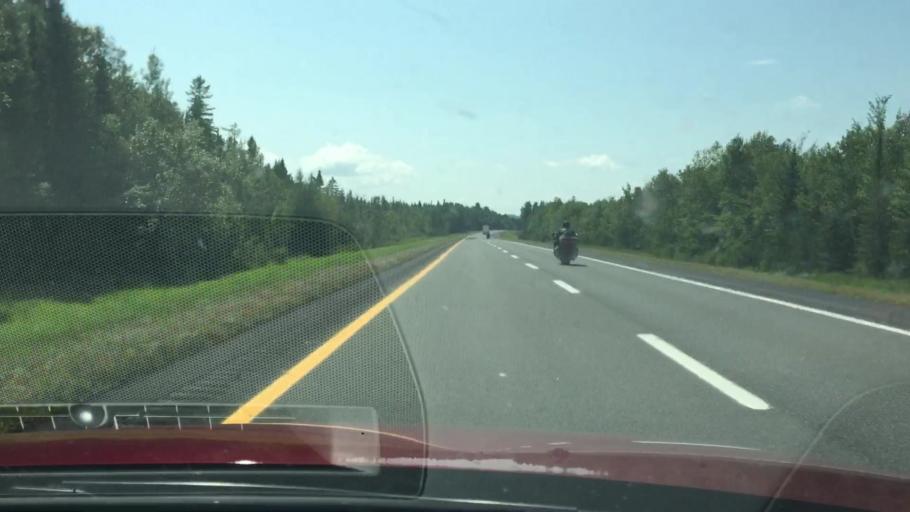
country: US
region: Maine
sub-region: Penobscot County
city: Patten
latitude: 45.9768
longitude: -68.2935
